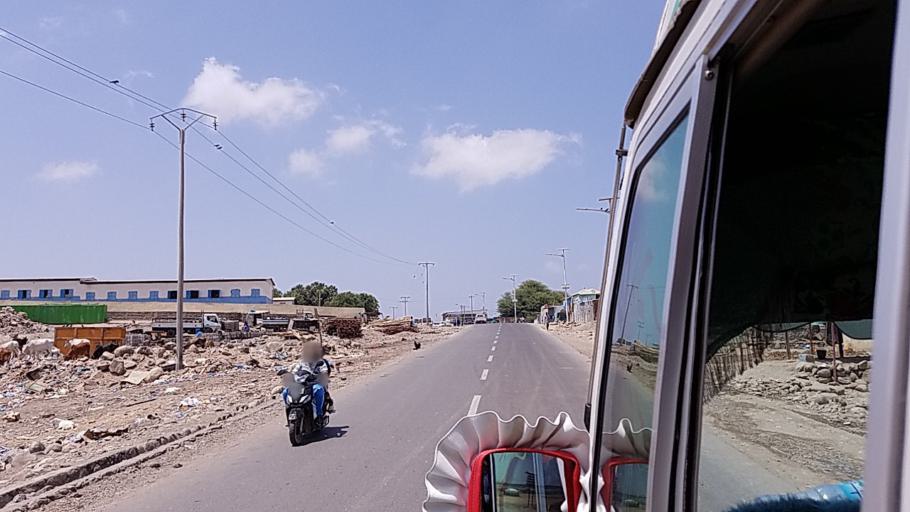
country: DJ
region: Djibouti
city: Djibouti
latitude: 11.5509
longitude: 43.1020
